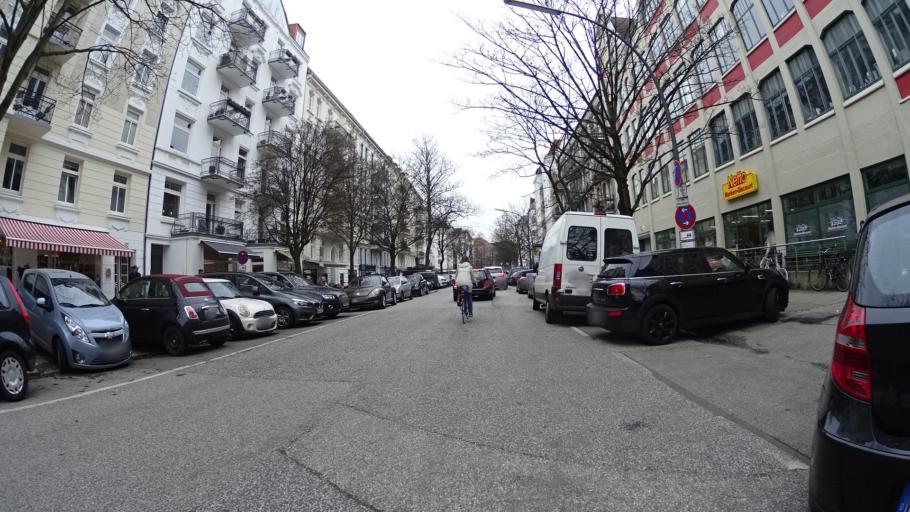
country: DE
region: Hamburg
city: Hamburg-Nord
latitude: 53.5831
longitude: 9.9815
